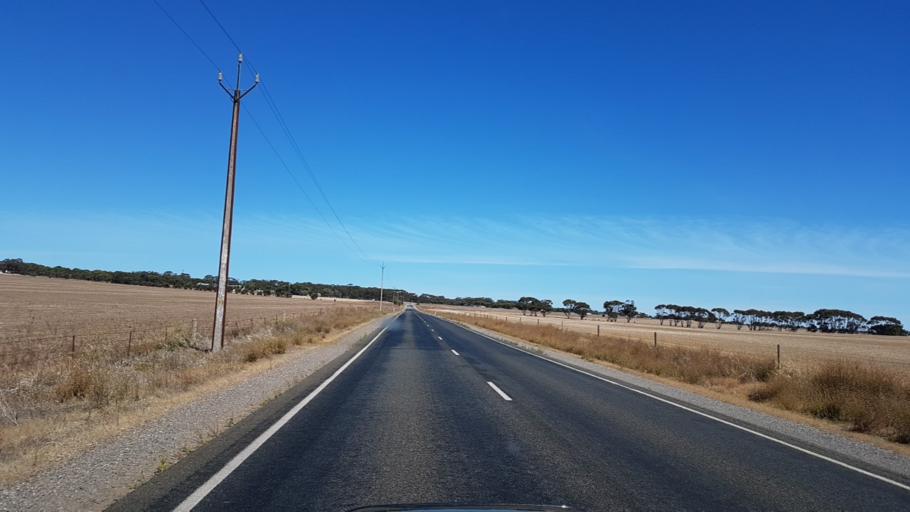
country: AU
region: South Australia
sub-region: Yorke Peninsula
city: Maitland
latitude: -34.3577
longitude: 137.6653
